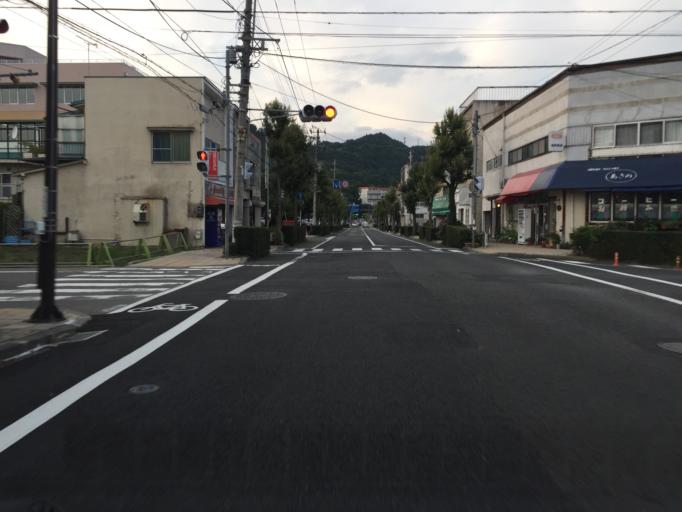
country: JP
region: Fukushima
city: Fukushima-shi
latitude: 37.7613
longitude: 140.4684
